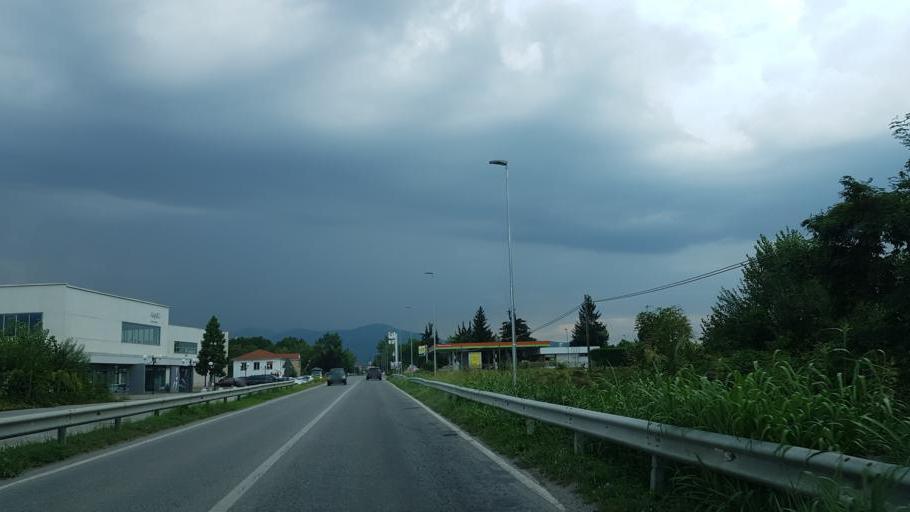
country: IT
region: Piedmont
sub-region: Provincia di Cuneo
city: Caraglio
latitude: 44.4074
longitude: 7.4431
